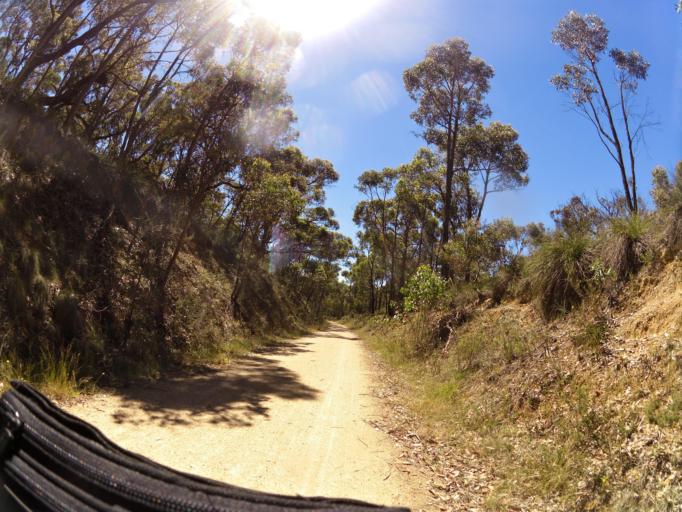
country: AU
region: Victoria
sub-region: Ballarat North
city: Delacombe
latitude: -37.7102
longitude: 143.6163
